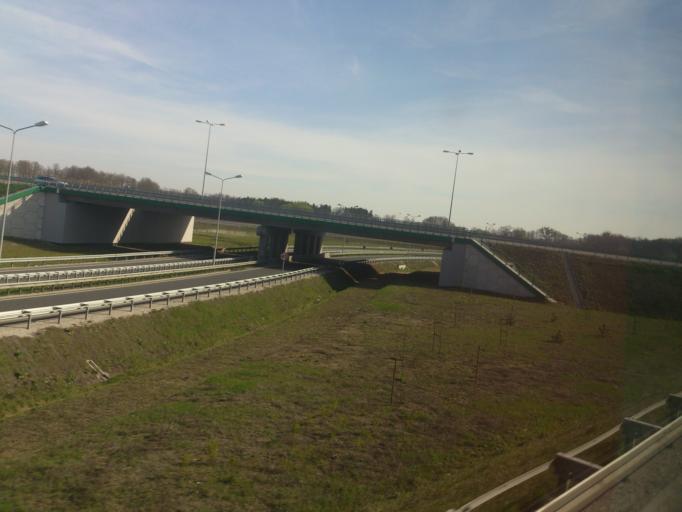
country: PL
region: Kujawsko-Pomorskie
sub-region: Powiat aleksandrowski
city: Ciechocinek
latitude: 52.8657
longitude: 18.7590
